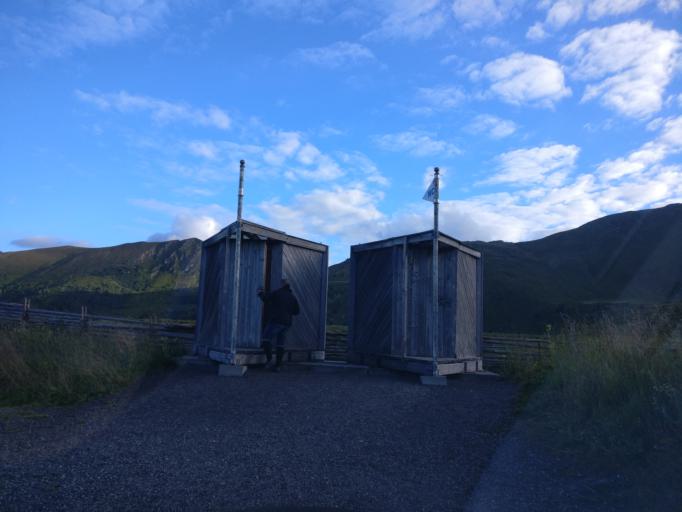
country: AT
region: Carinthia
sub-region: Politischer Bezirk Spittal an der Drau
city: Kleinkirchheim
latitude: 46.8876
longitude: 13.8036
